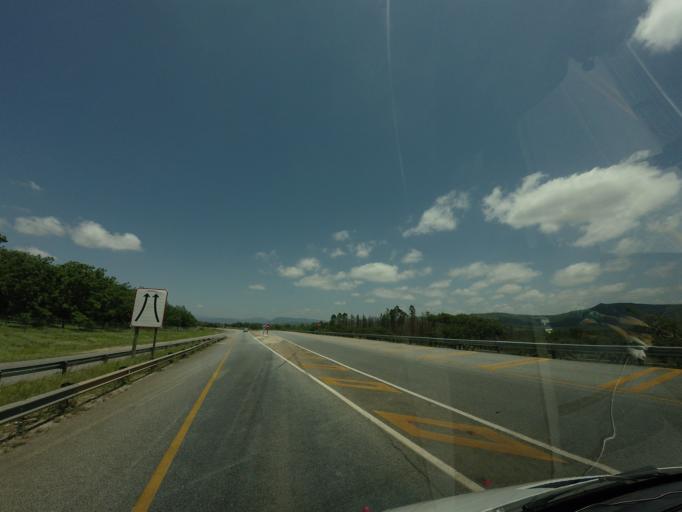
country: ZA
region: Mpumalanga
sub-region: Ehlanzeni District
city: Nelspruit
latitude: -25.4466
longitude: 30.9166
